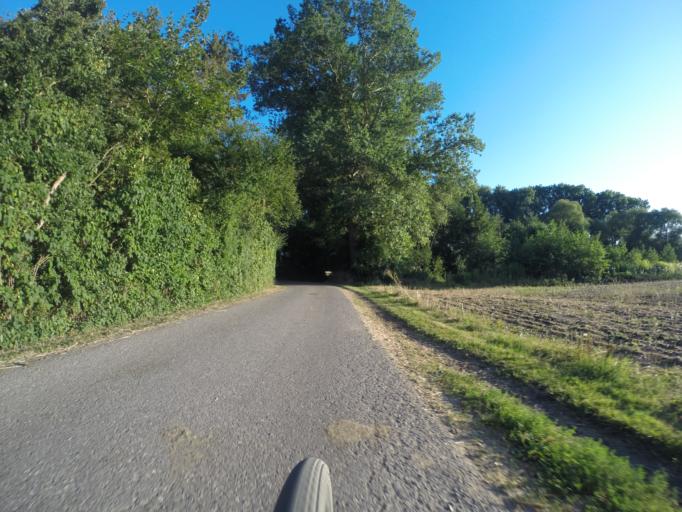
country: DK
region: Capital Region
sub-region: Ballerup Kommune
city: Ballerup
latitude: 55.7021
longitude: 12.3304
